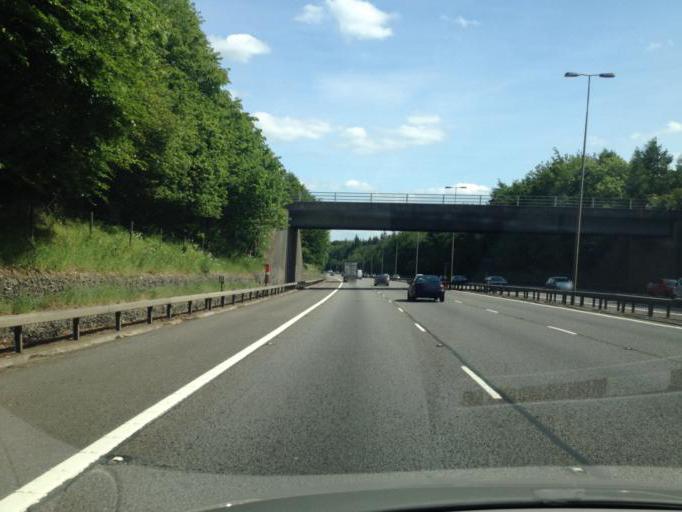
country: GB
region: England
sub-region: Buckinghamshire
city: Stokenchurch
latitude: 51.6358
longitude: -0.8811
